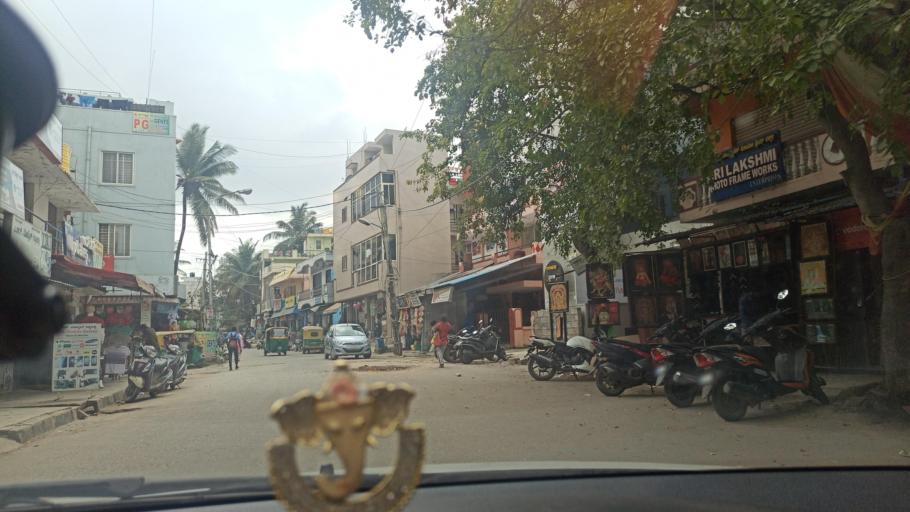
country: IN
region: Karnataka
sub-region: Bangalore Urban
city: Bangalore
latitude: 12.9229
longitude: 77.6498
